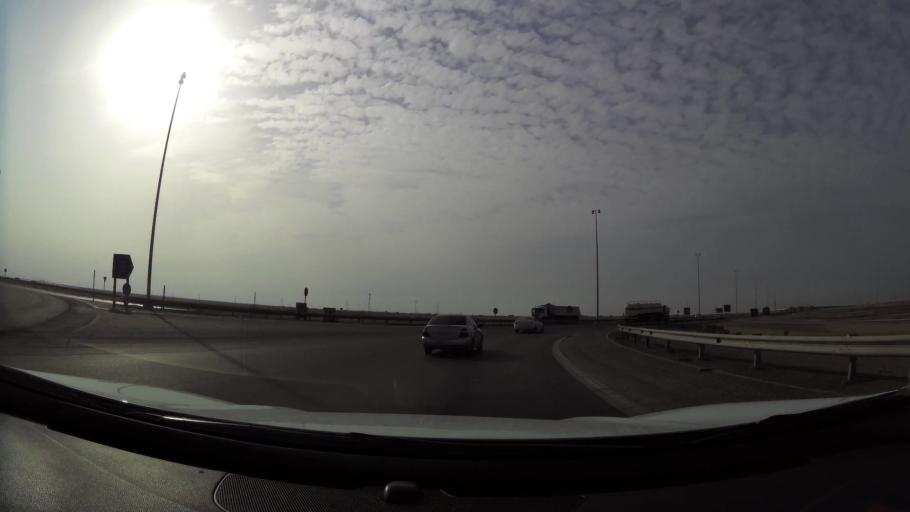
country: AE
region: Abu Dhabi
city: Abu Dhabi
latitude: 24.2039
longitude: 54.4201
